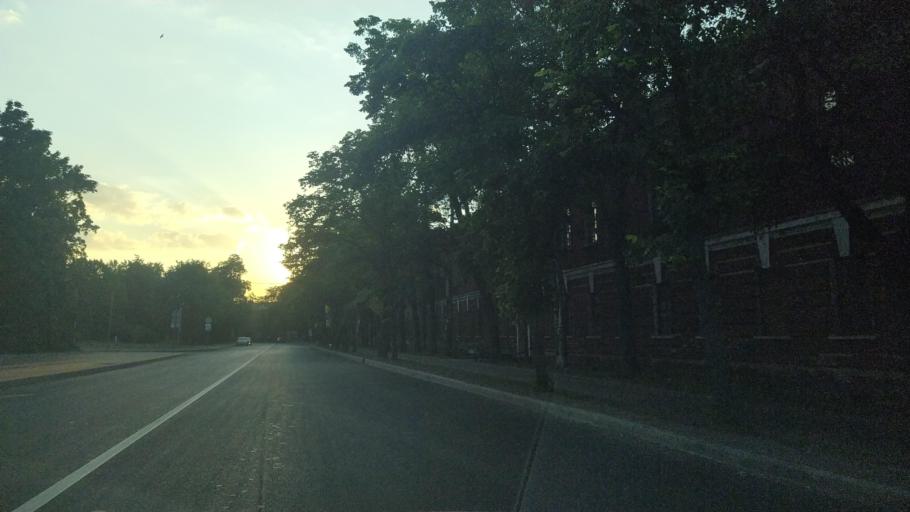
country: RU
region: St.-Petersburg
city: Kronshtadt
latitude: 60.0015
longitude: 29.7677
